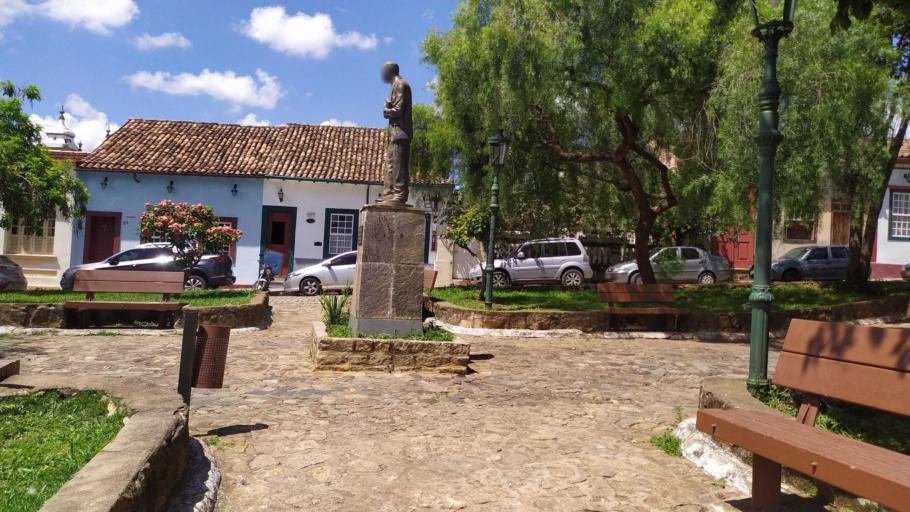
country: BR
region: Minas Gerais
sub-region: Sao Joao Del Rei
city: Sao Joao del Rei
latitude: -21.1338
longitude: -44.2618
